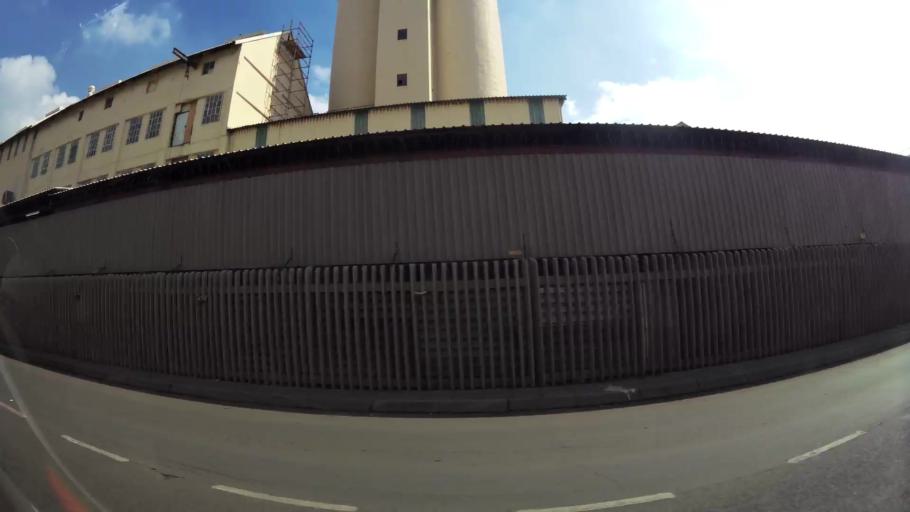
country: ZA
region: Gauteng
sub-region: Sedibeng District Municipality
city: Vereeniging
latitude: -26.6706
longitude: 27.9348
